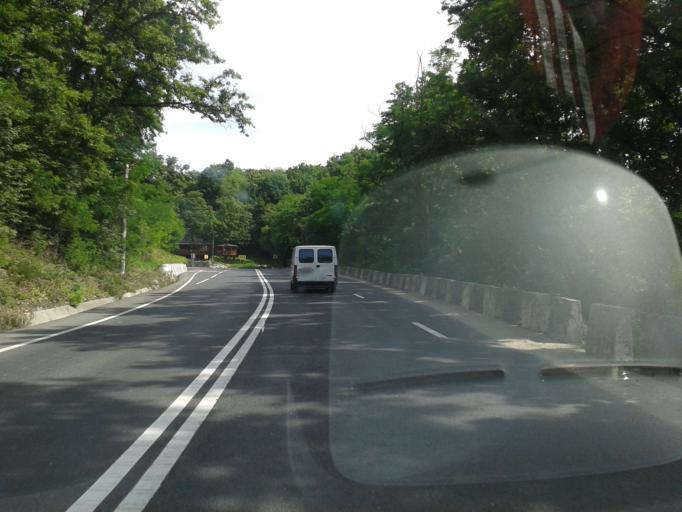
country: RO
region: Hunedoara
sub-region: Oras Hateg
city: Hateg
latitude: 45.6143
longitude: 22.9756
